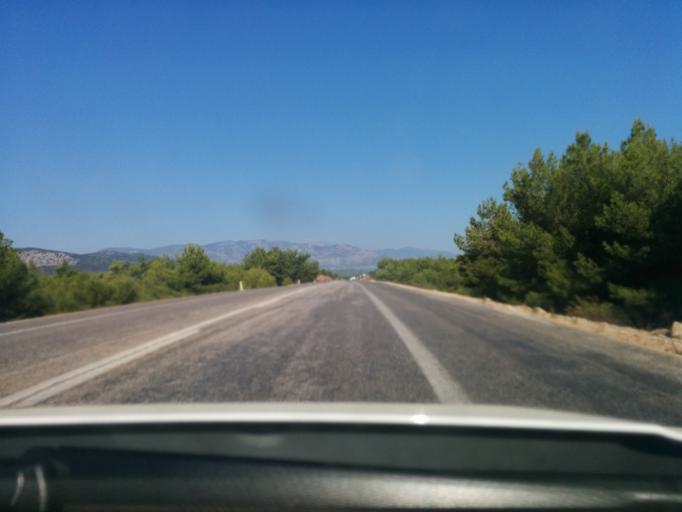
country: TR
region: Mugla
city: Esen
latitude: 36.3683
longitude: 29.3270
